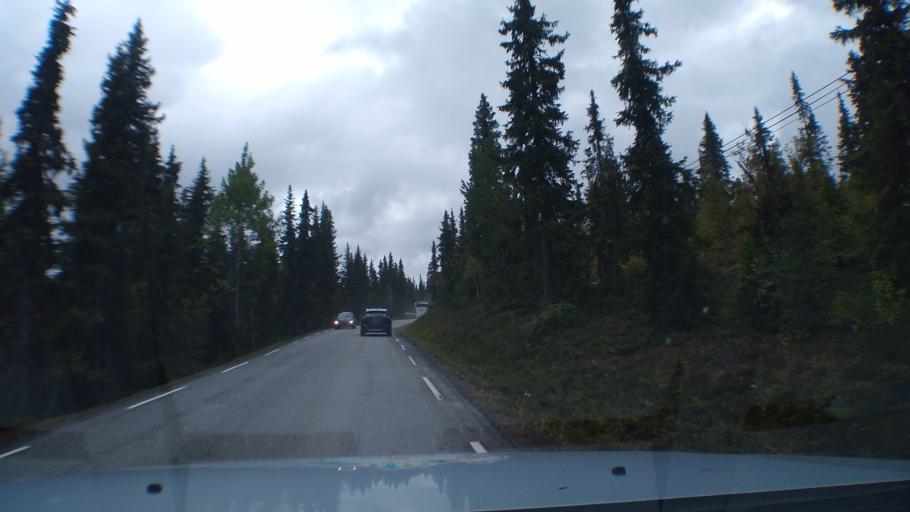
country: NO
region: Oppland
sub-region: Ringebu
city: Ringebu
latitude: 61.6023
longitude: 10.0684
